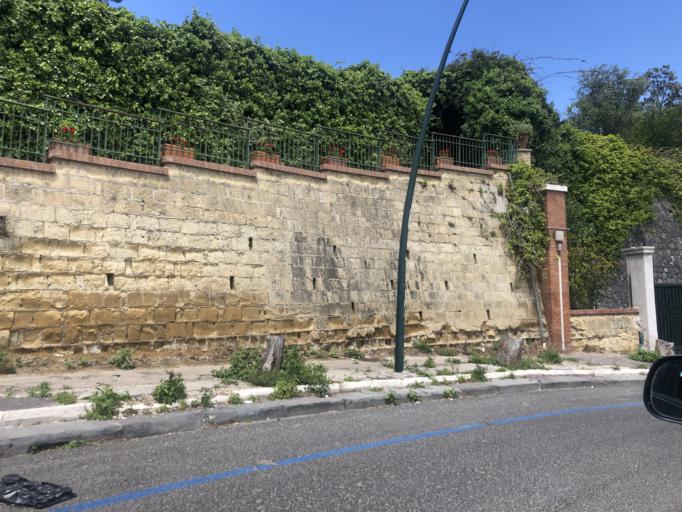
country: IT
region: Campania
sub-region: Provincia di Napoli
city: Bagnoli
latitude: 40.8003
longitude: 14.1841
